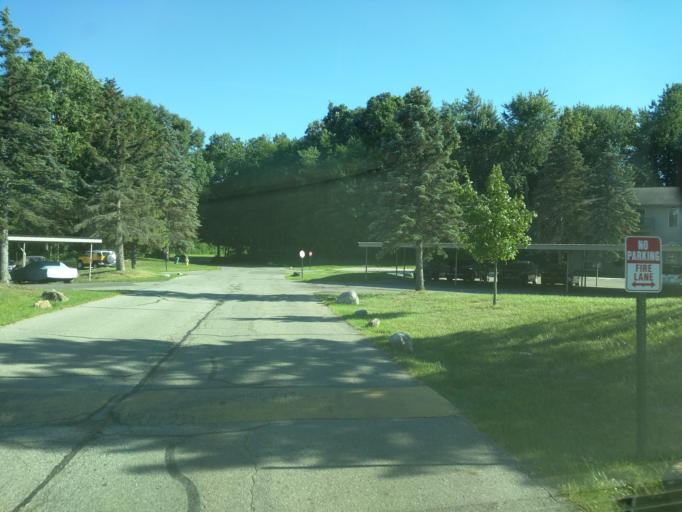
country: US
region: Michigan
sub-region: Eaton County
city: Waverly
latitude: 42.7364
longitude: -84.6386
